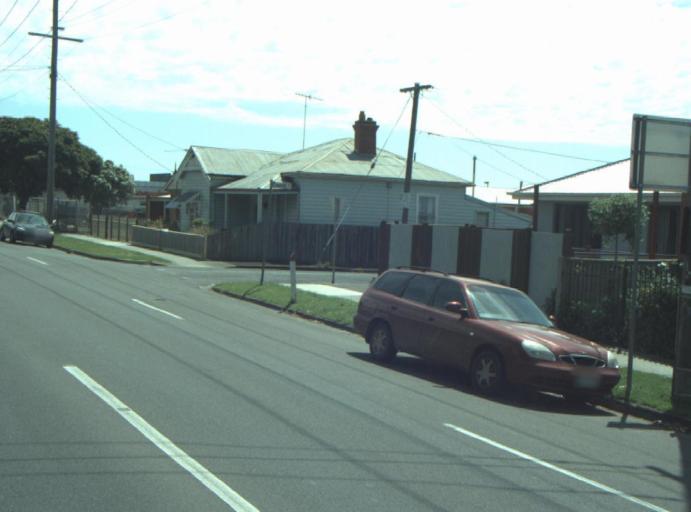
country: AU
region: Victoria
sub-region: Greater Geelong
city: Geelong West
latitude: -38.1405
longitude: 144.3364
